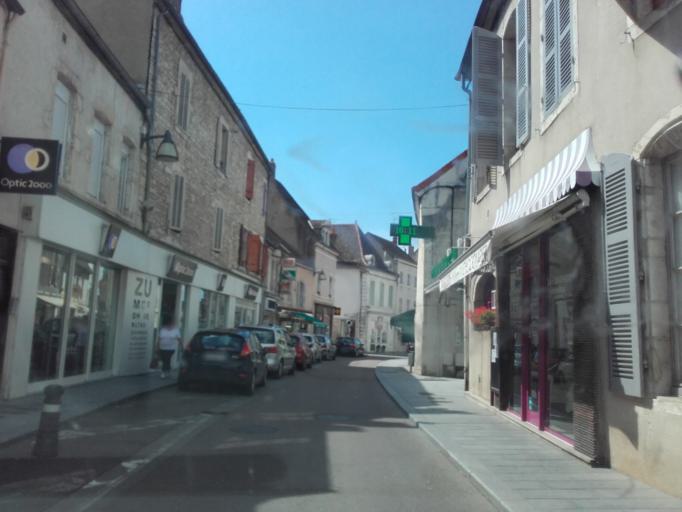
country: FR
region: Bourgogne
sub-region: Departement de Saone-et-Loire
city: Chagny
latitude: 46.9098
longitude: 4.7531
